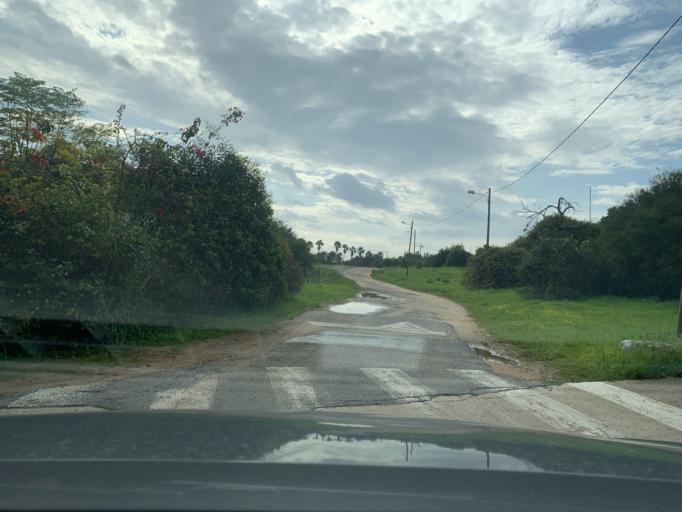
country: PS
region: West Bank
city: Qalqilyah
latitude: 32.1972
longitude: 34.9466
